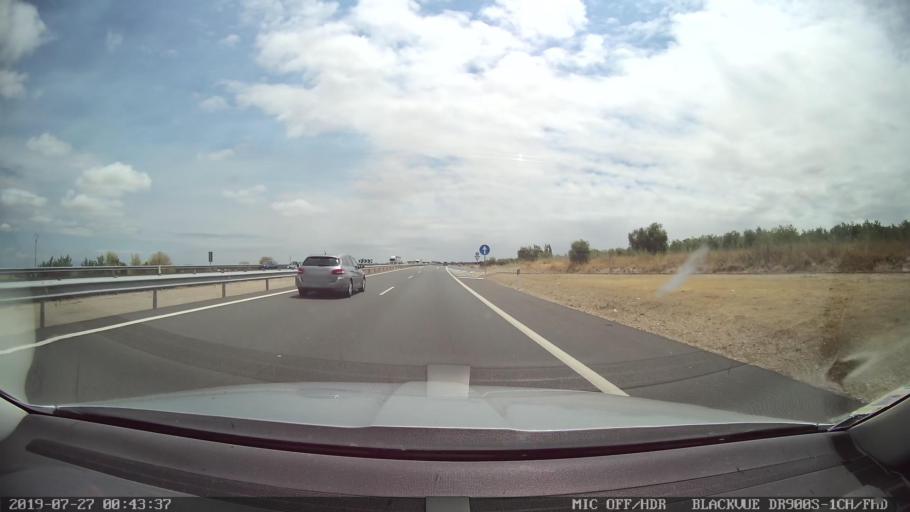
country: ES
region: Castille-La Mancha
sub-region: Province of Toledo
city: Torralba de Oropesa
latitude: 39.9303
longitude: -5.1400
